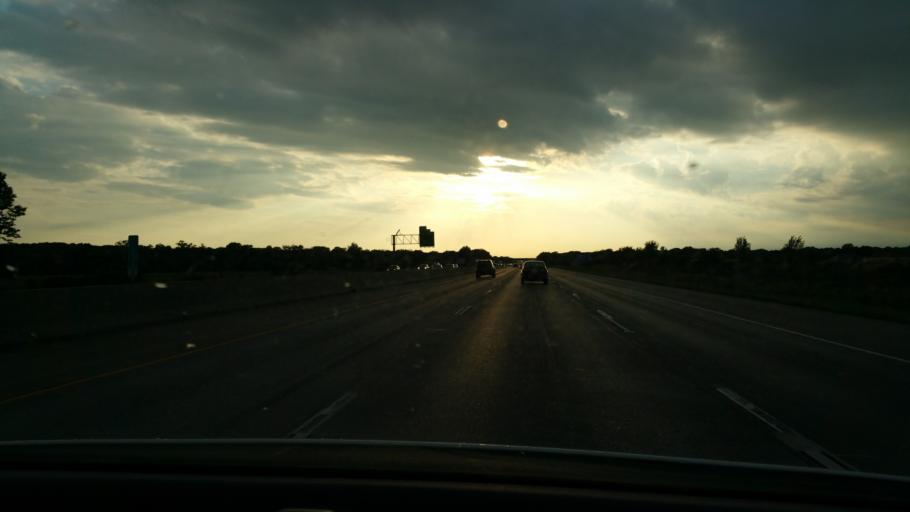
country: US
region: Iowa
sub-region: Polk County
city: Saylorville
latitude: 41.6497
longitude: -93.6429
